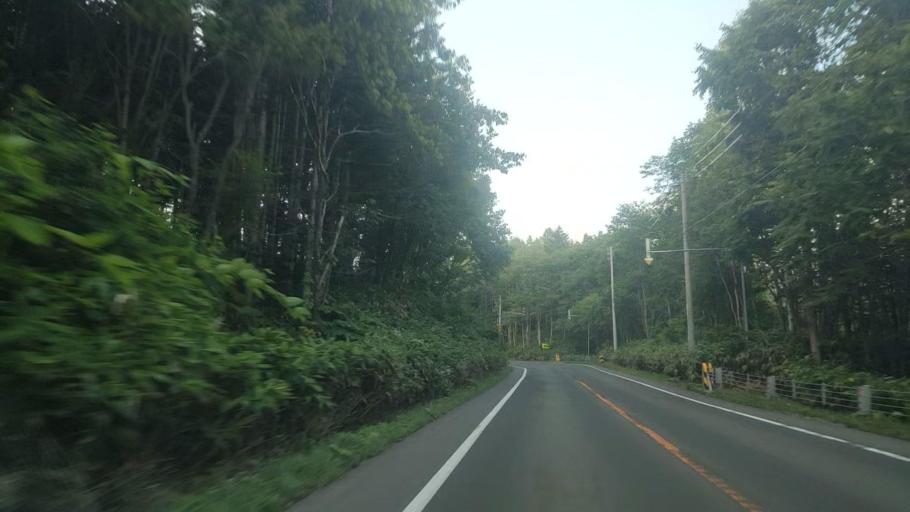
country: JP
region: Hokkaido
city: Bibai
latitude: 43.2602
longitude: 142.0295
